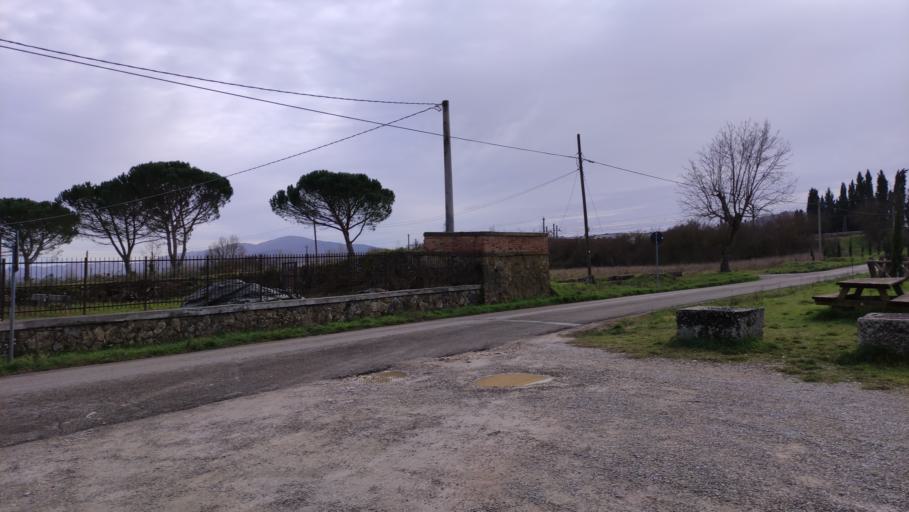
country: IT
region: Tuscany
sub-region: Province of Arezzo
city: Pratantico-Indicatore
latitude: 43.4678
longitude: 11.8254
